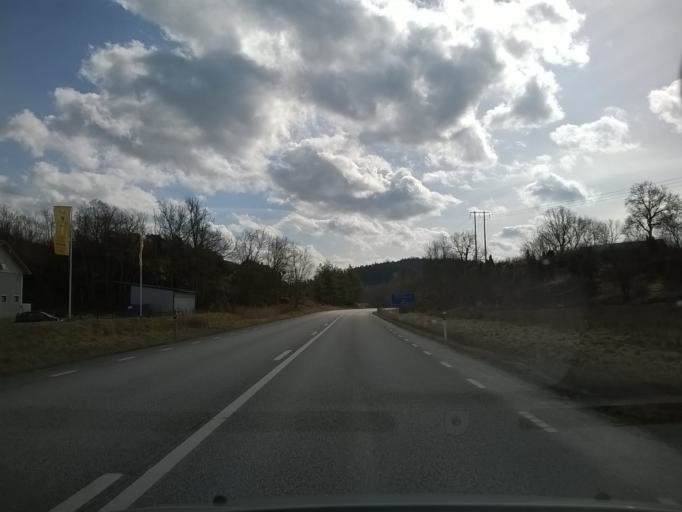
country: SE
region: Vaestra Goetaland
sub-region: Tjorns Kommun
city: Myggenas
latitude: 58.1295
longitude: 11.7217
